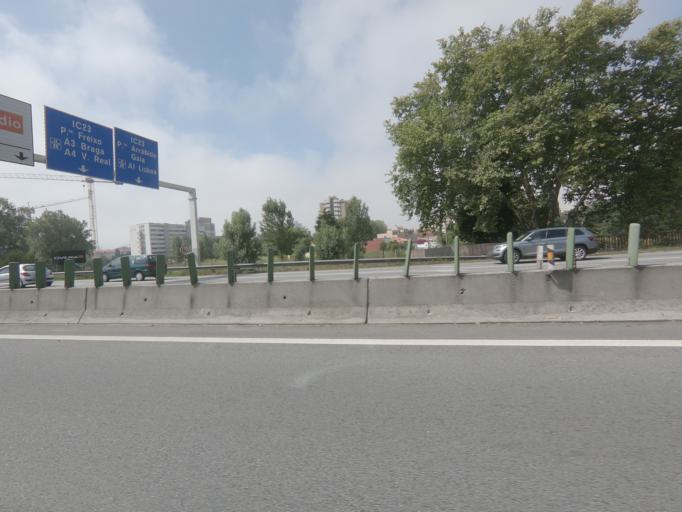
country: PT
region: Porto
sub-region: Matosinhos
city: Senhora da Hora
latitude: 41.1690
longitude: -8.6443
